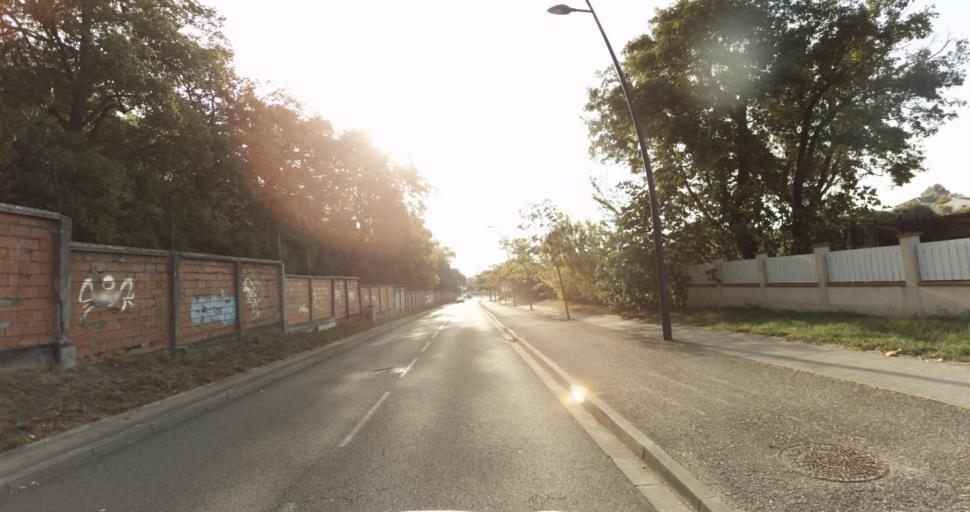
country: FR
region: Midi-Pyrenees
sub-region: Departement de la Haute-Garonne
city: Ramonville-Saint-Agne
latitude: 43.5384
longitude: 1.4659
